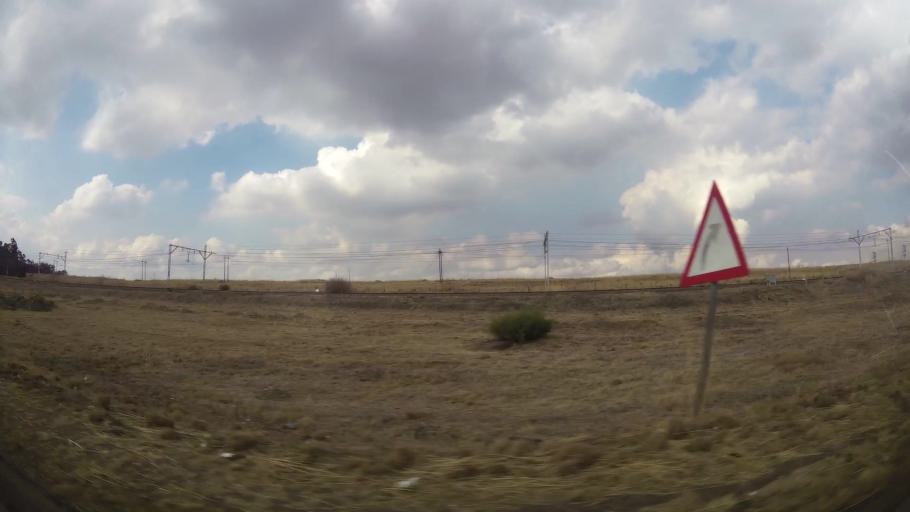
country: ZA
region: Gauteng
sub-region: Sedibeng District Municipality
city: Vereeniging
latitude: -26.7005
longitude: 27.9342
